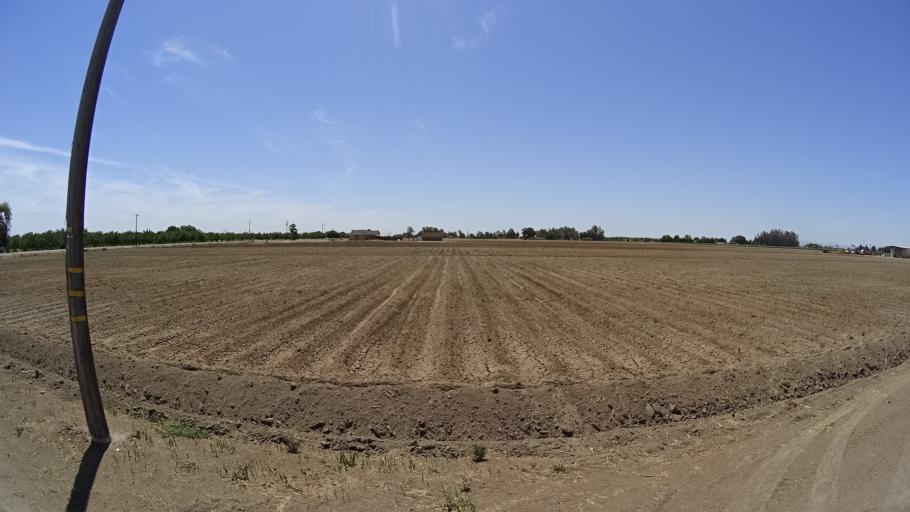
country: US
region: California
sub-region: Kings County
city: Lemoore
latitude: 36.3498
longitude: -119.7821
